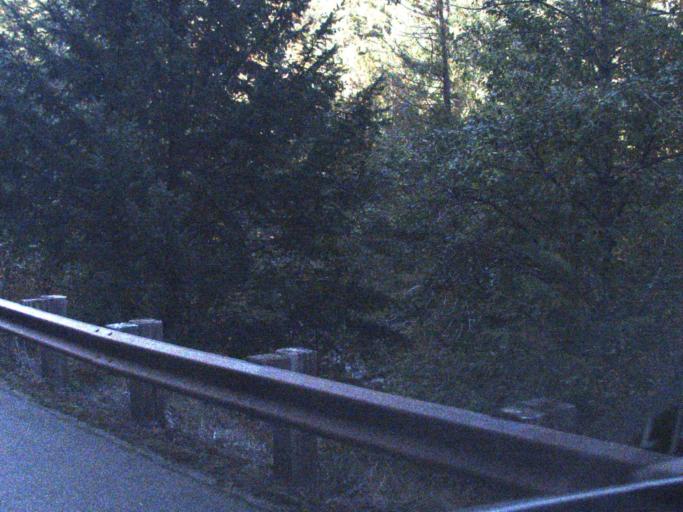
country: US
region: Washington
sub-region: Snohomish County
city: Darrington
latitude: 48.7047
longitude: -120.9405
